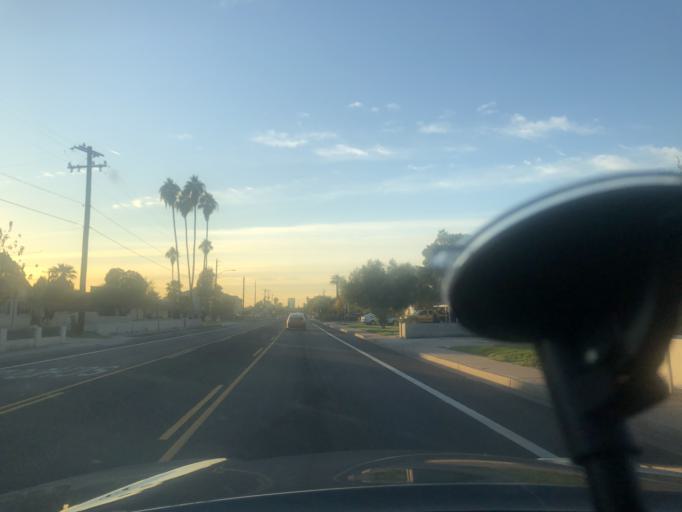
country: US
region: Arizona
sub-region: Maricopa County
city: Phoenix
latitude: 33.4876
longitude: -112.0356
